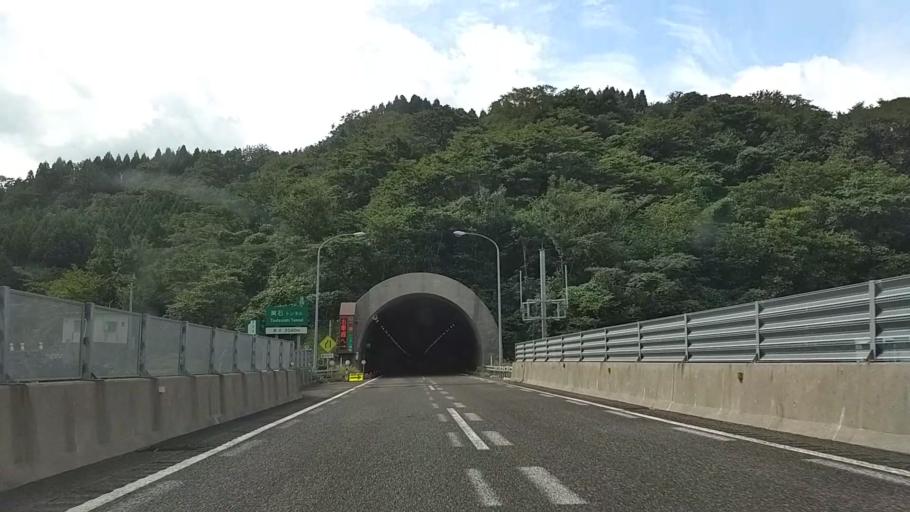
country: JP
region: Niigata
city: Joetsu
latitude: 37.1304
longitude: 138.0591
